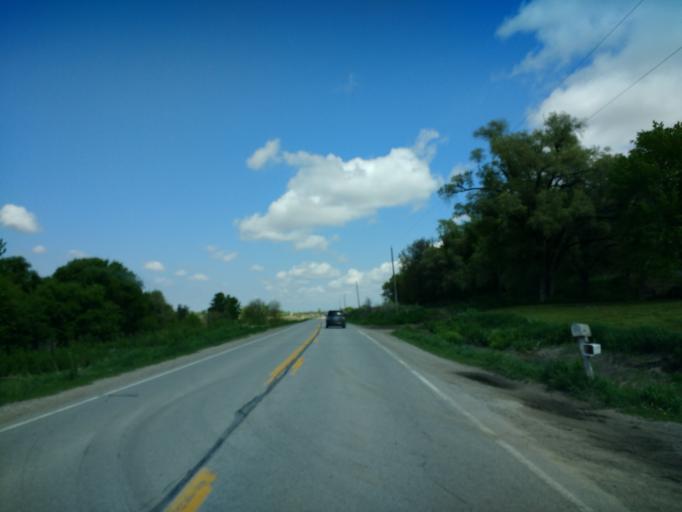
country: US
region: Iowa
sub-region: Harrison County
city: Missouri Valley
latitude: 41.4847
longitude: -95.8855
